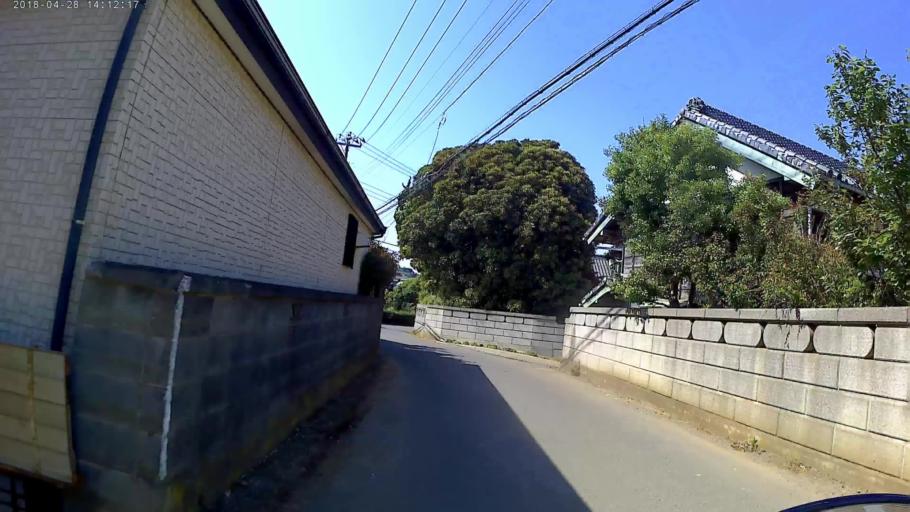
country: JP
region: Kanagawa
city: Miura
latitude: 35.1461
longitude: 139.6518
